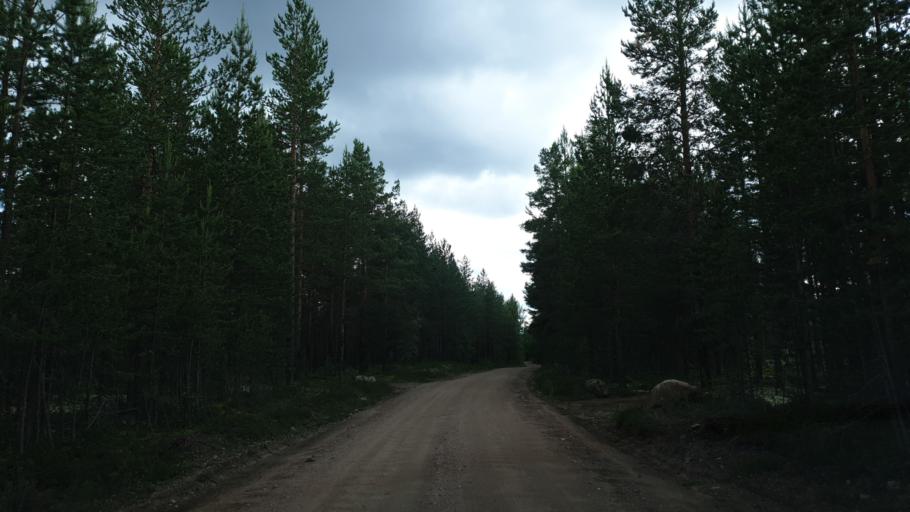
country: SE
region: Jaemtland
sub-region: Harjedalens Kommun
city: Sveg
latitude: 62.0247
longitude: 14.4706
